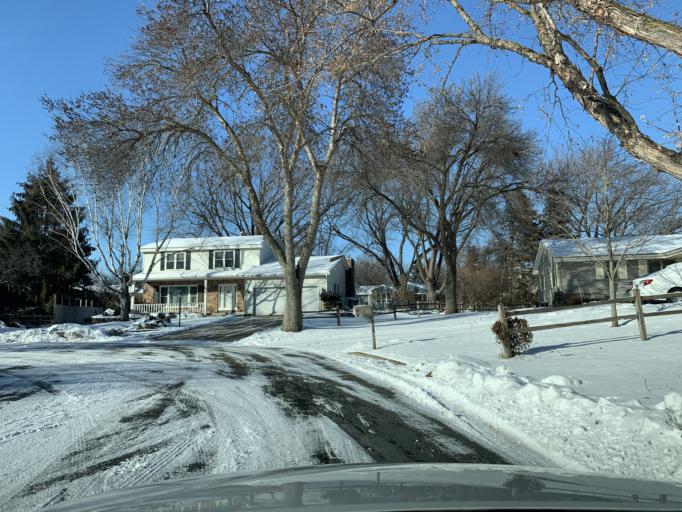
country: US
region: Minnesota
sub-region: Scott County
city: Savage
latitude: 44.8218
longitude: -93.3410
